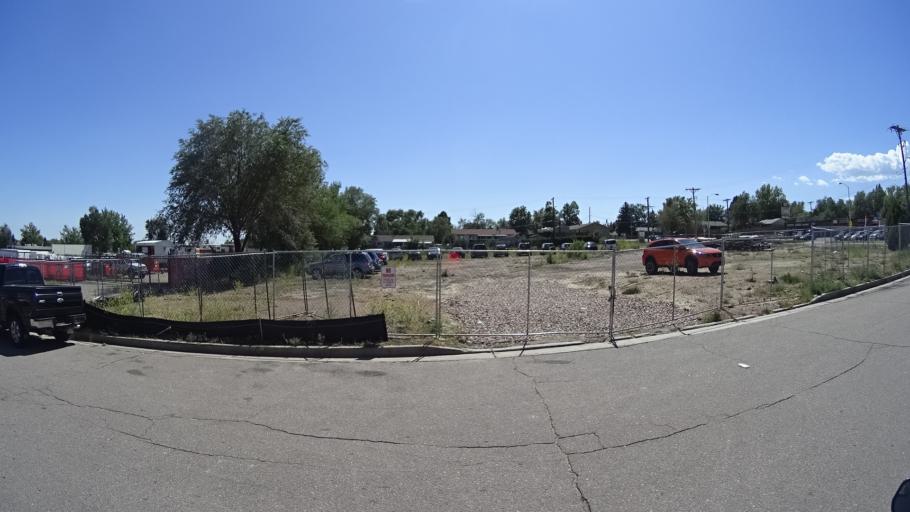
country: US
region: Colorado
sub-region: El Paso County
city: Colorado Springs
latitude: 38.8371
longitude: -104.7660
